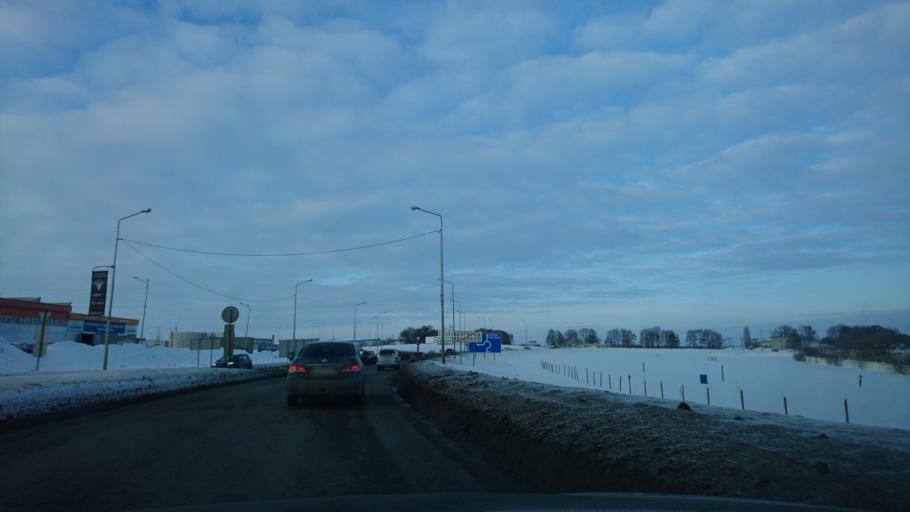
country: RU
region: Belgorod
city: Severnyy
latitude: 50.6583
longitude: 36.5642
